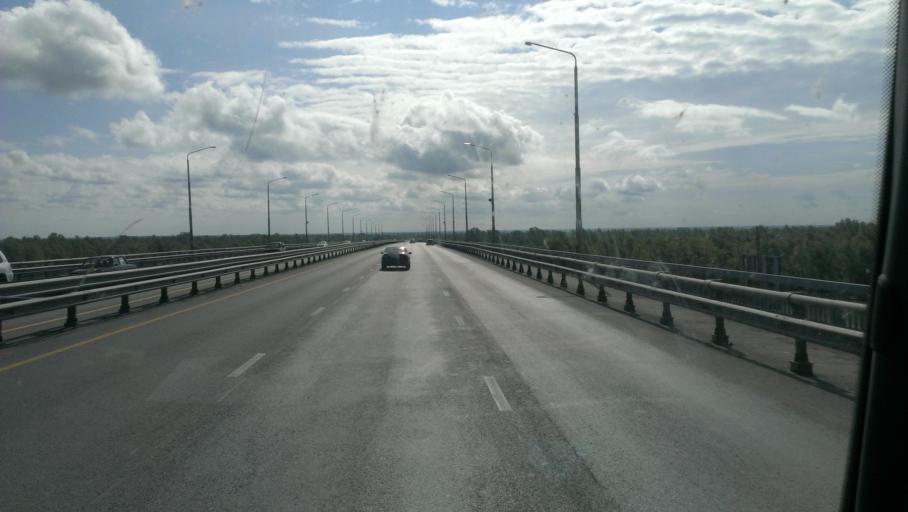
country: RU
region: Altai Krai
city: Zaton
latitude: 53.3233
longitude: 83.8038
